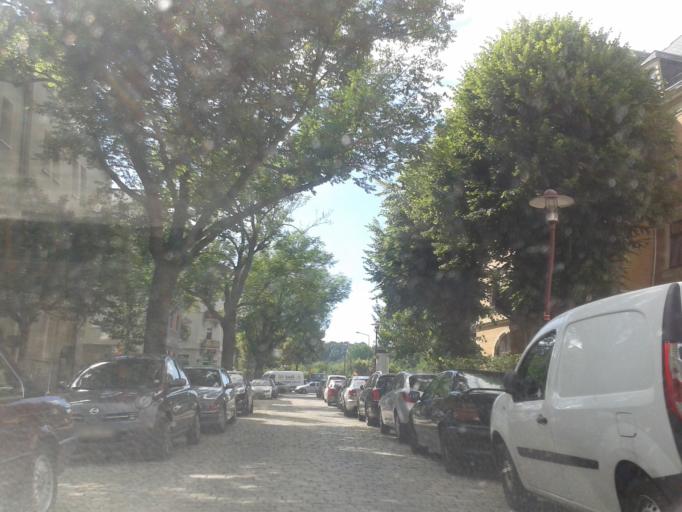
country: DE
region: Saxony
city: Radebeul
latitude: 51.0520
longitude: 13.6783
